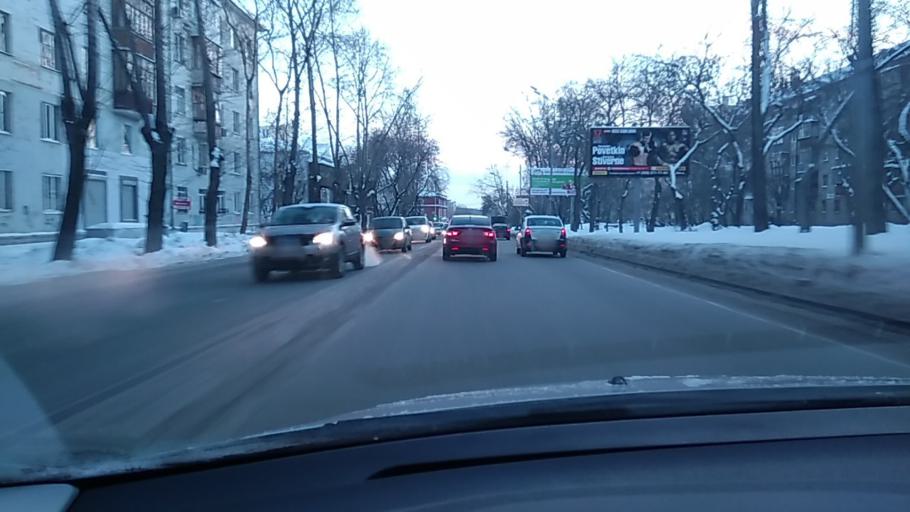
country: RU
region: Sverdlovsk
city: Yekaterinburg
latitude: 56.8250
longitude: 60.6383
